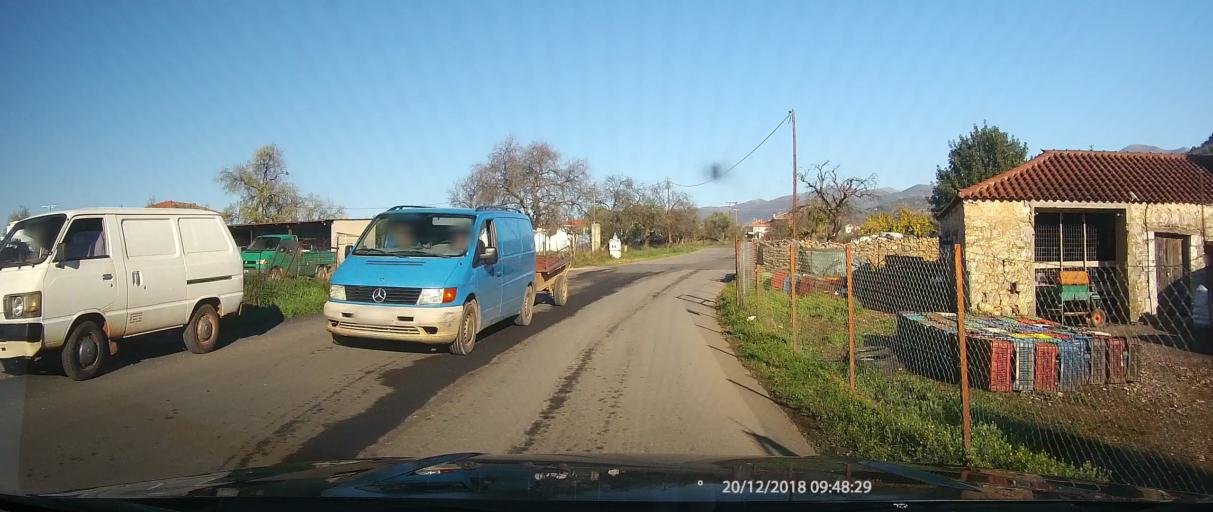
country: GR
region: Peloponnese
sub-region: Nomos Lakonias
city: Yerakion
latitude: 36.9910
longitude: 22.7017
